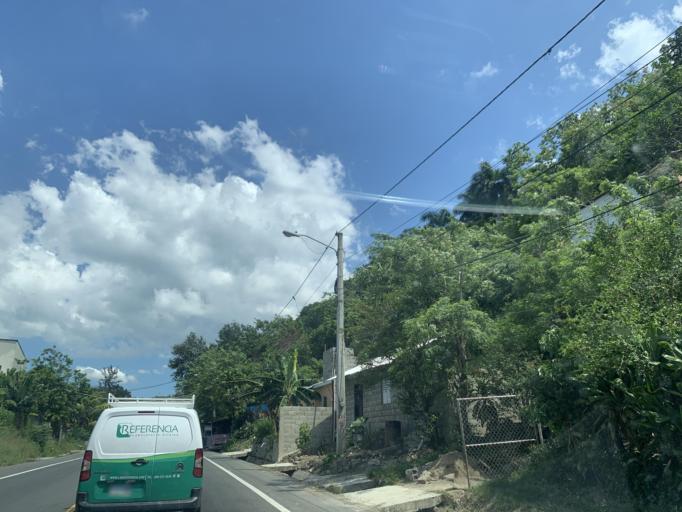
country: DO
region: Puerto Plata
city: Altamira
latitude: 19.6696
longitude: -70.8326
